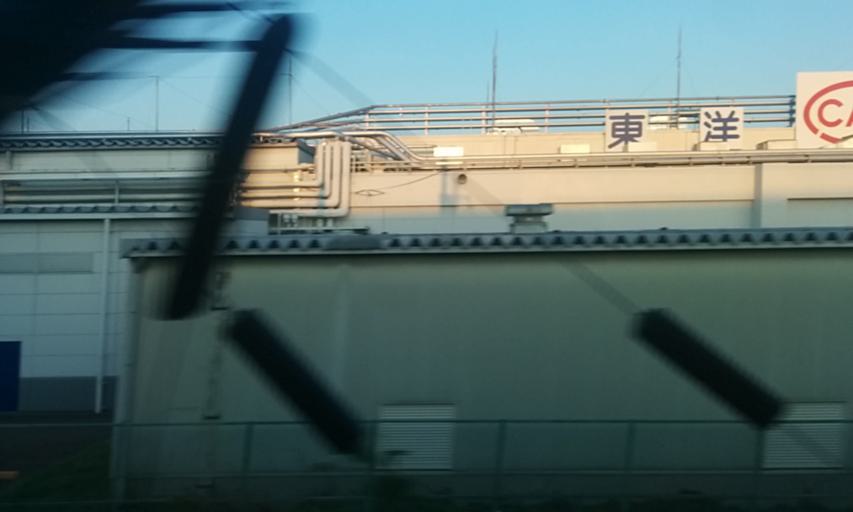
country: JP
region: Osaka
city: Ibaraki
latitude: 34.8067
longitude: 135.5584
